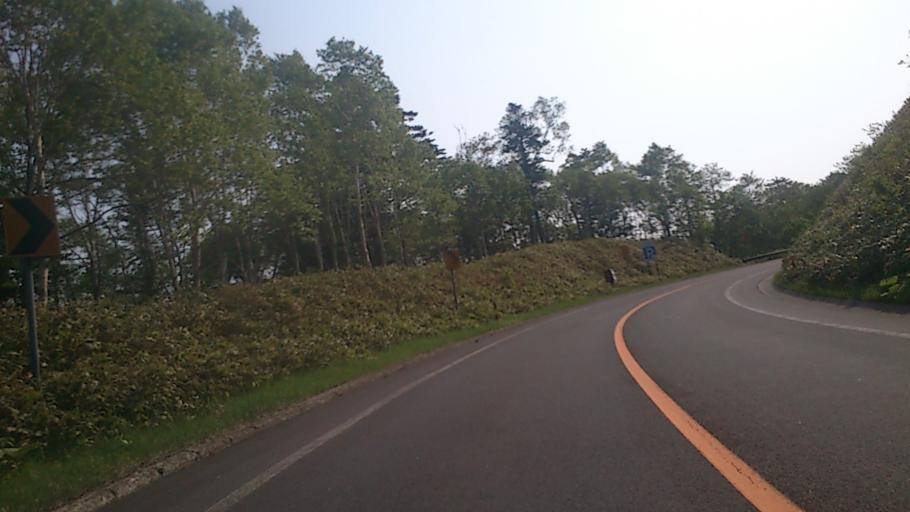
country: JP
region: Hokkaido
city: Bihoro
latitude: 43.4488
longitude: 144.2002
